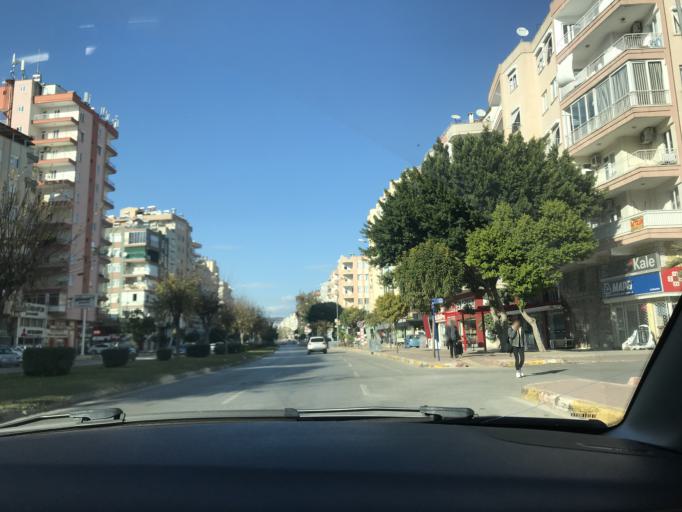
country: TR
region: Antalya
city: Antalya
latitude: 36.9038
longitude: 30.7009
